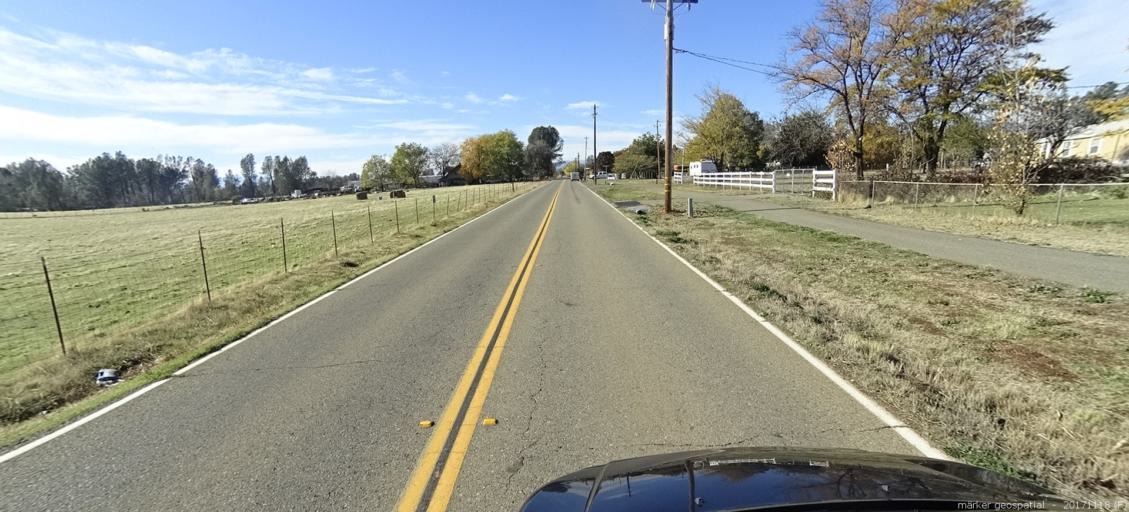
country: US
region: California
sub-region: Shasta County
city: Anderson
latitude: 40.4393
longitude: -122.4023
